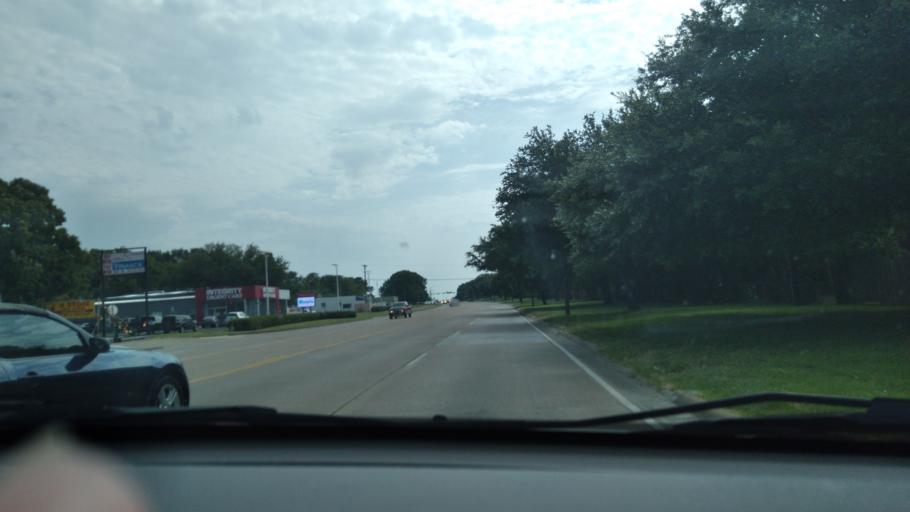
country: US
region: Texas
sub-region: Navarro County
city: Corsicana
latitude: 32.0778
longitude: -96.4927
